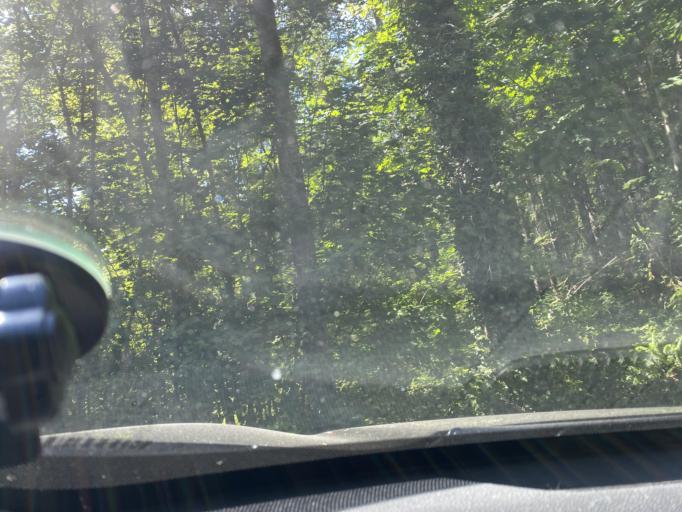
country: US
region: Washington
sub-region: Snohomish County
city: Sultan
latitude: 47.9053
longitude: -121.8398
